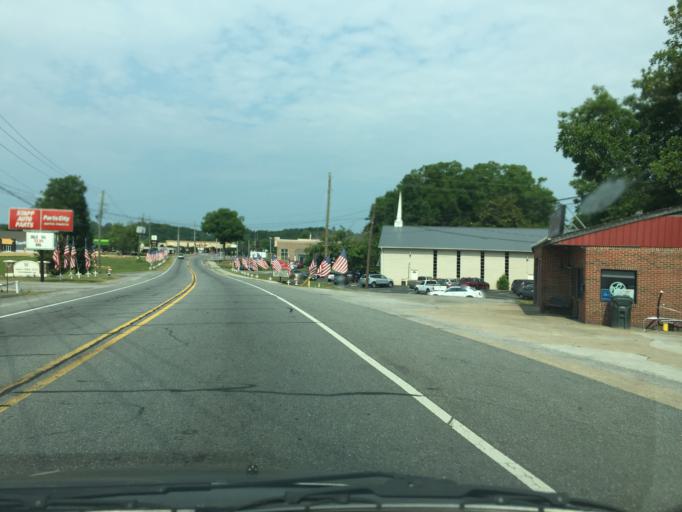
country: US
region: Georgia
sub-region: Catoosa County
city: Ringgold
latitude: 34.9187
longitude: -85.1198
